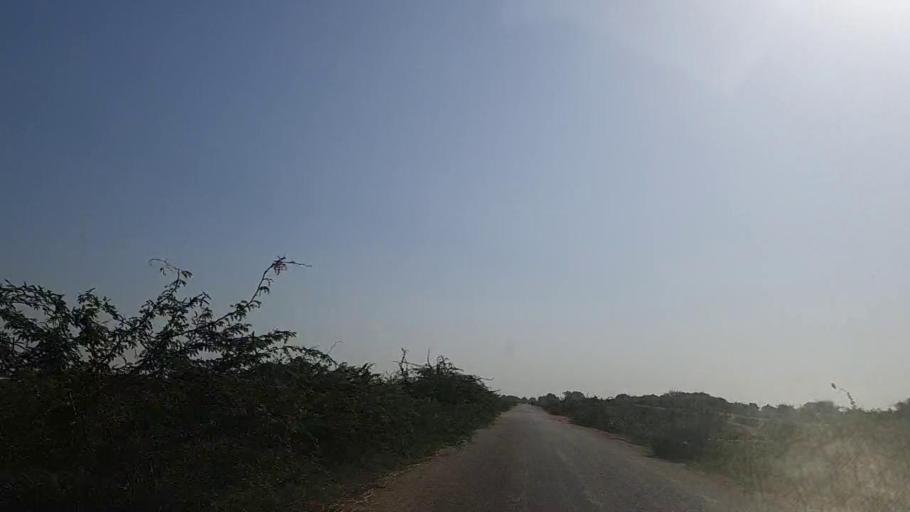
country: PK
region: Sindh
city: Jati
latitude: 24.4321
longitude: 68.2593
